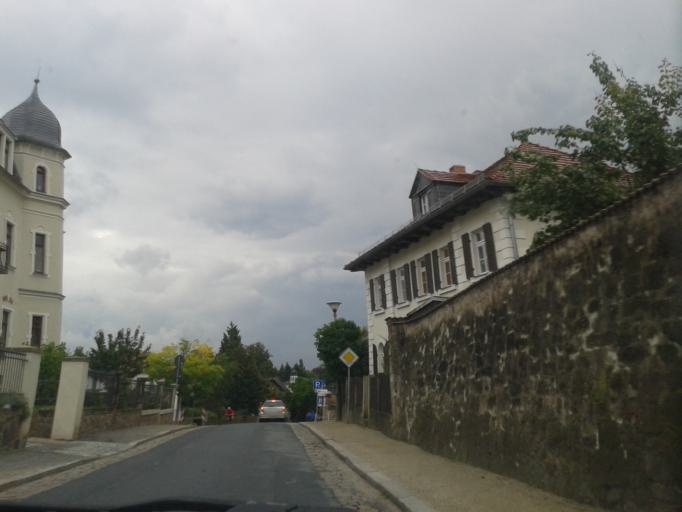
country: DE
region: Saxony
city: Radebeul
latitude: 51.1087
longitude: 13.6585
